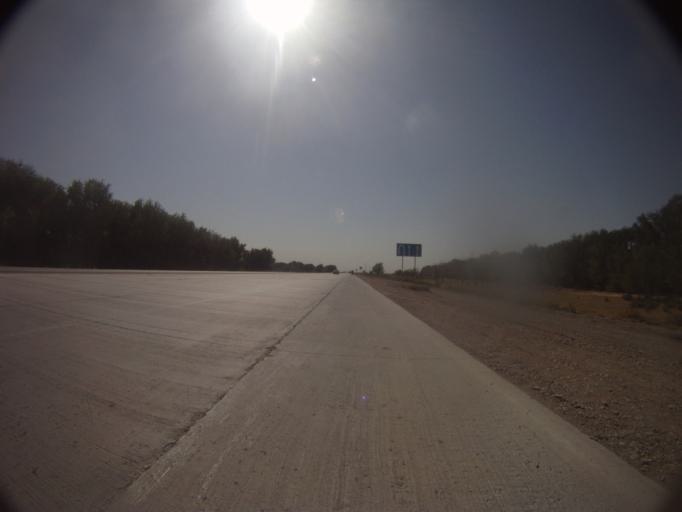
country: KZ
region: Ongtustik Qazaqstan
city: Turkestan
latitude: 43.1507
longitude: 68.5726
